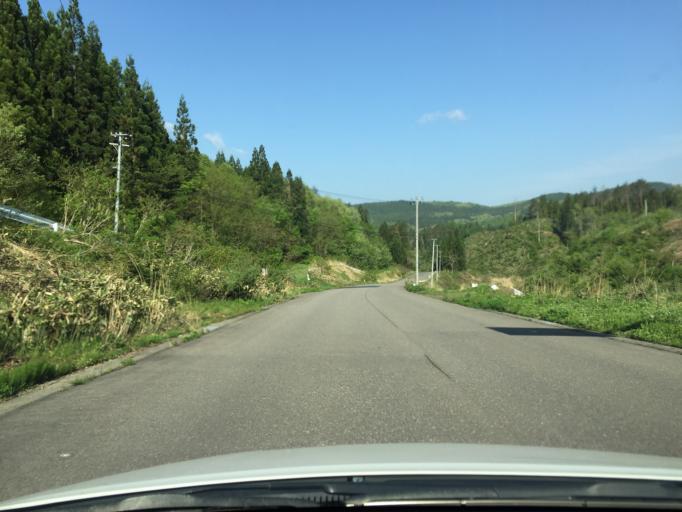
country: JP
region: Fukushima
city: Kitakata
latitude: 37.6726
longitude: 139.6306
